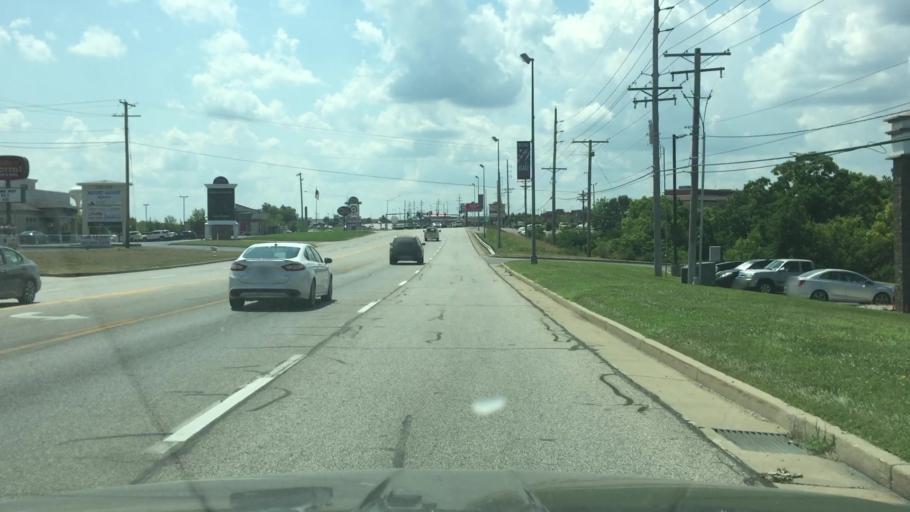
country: US
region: Missouri
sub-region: Miller County
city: Lake Ozark
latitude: 38.1643
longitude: -92.6095
